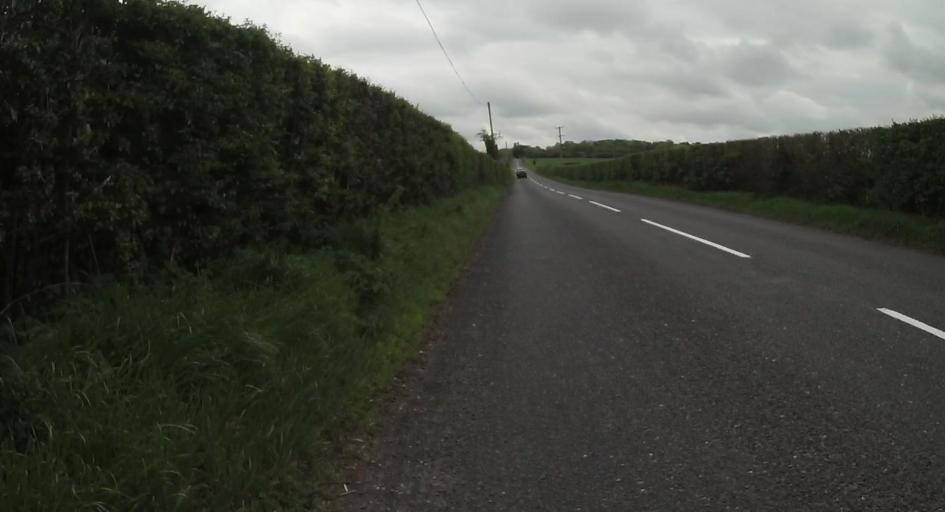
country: GB
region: England
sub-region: Hampshire
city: Colden Common
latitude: 51.0171
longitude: -1.2551
